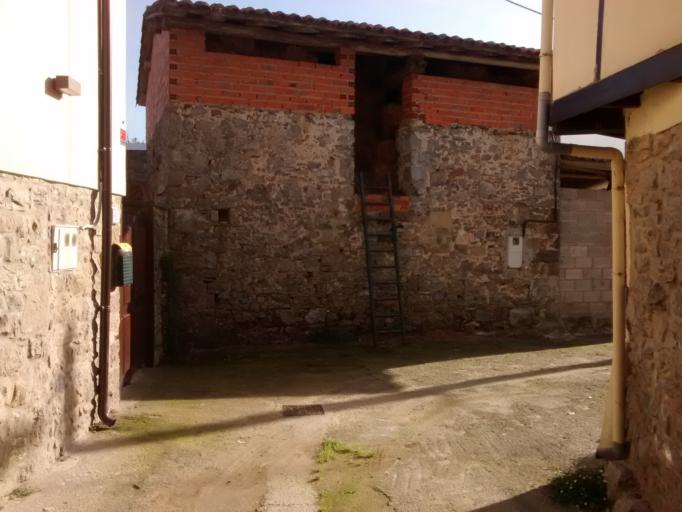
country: ES
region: Asturias
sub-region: Province of Asturias
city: Colunga
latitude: 43.4700
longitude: -5.2373
